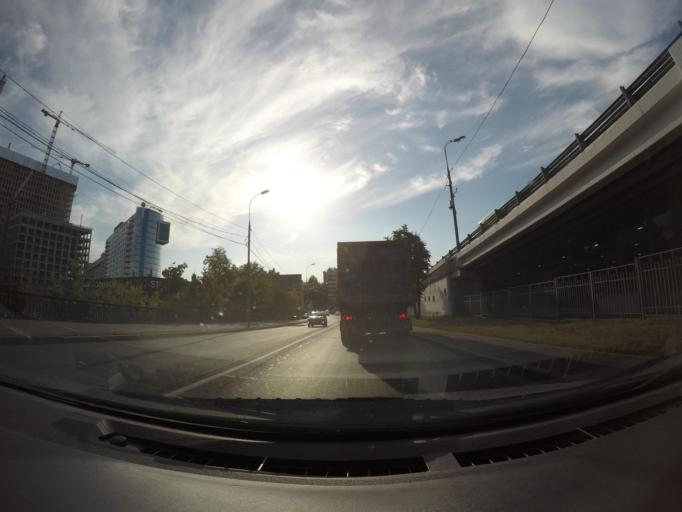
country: RU
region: Moscow
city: Mar'ina Roshcha
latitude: 55.7920
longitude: 37.5874
